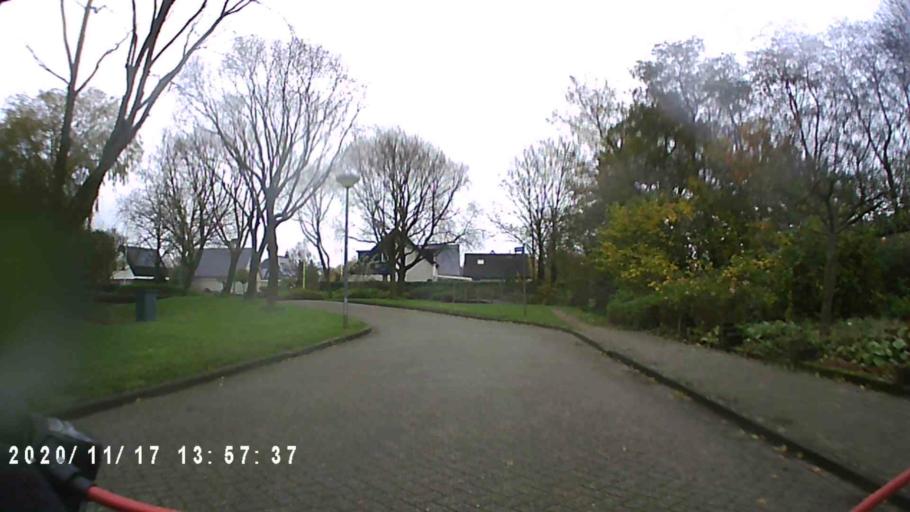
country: NL
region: Groningen
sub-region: Gemeente Zuidhorn
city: Grijpskerk
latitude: 53.2234
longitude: 6.3488
